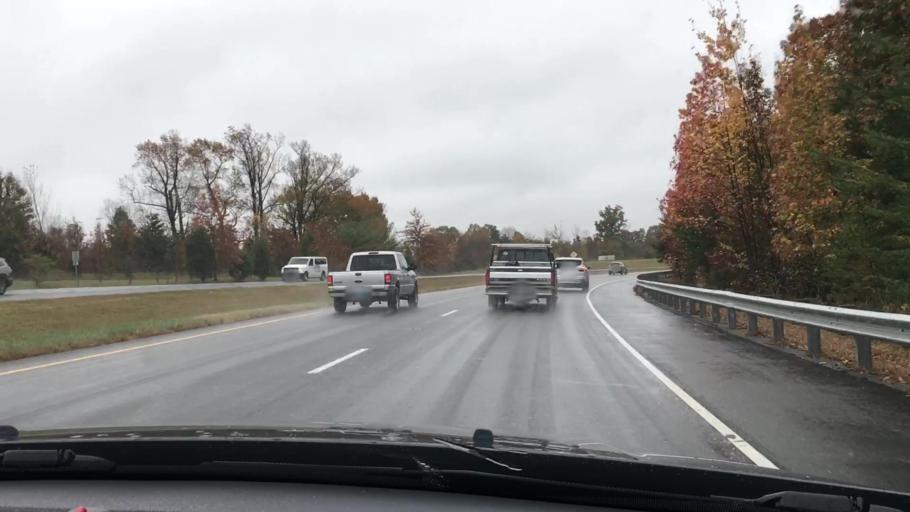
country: US
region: Virginia
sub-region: Prince William County
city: Lake Ridge
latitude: 38.7345
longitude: -77.2797
